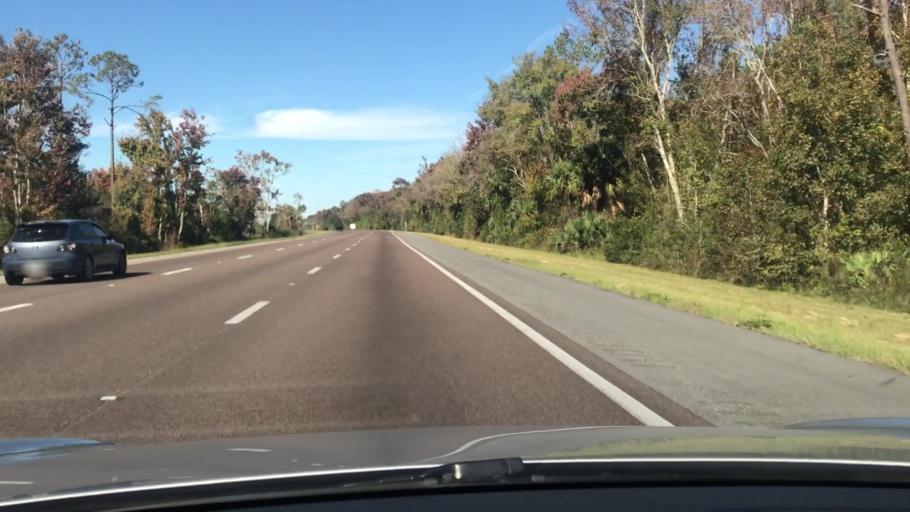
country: US
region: Florida
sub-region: Volusia County
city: Edgewater
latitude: 28.9230
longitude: -80.9378
